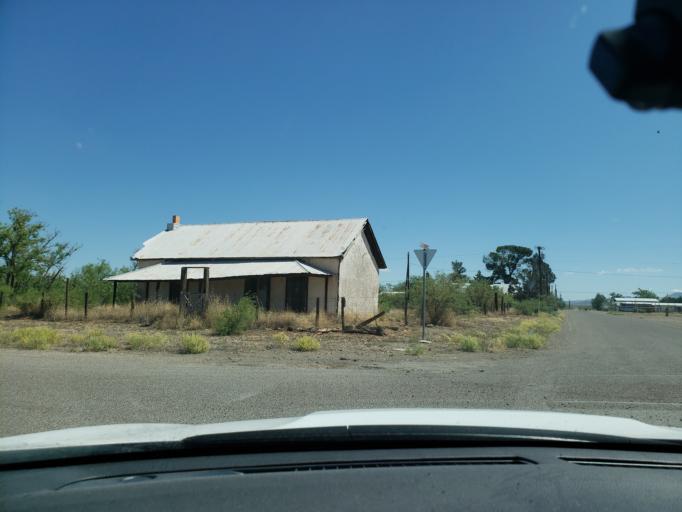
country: US
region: Texas
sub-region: Presidio County
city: Marfa
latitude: 30.5883
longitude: -104.4955
